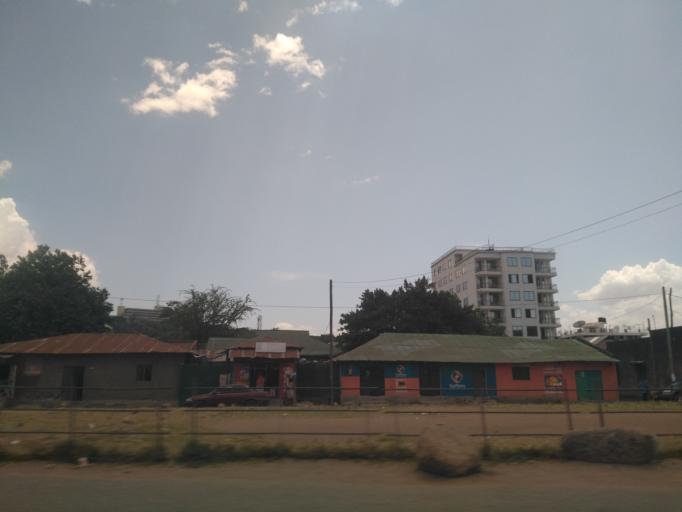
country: TZ
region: Mwanza
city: Mwanza
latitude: -2.5199
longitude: 32.9093
